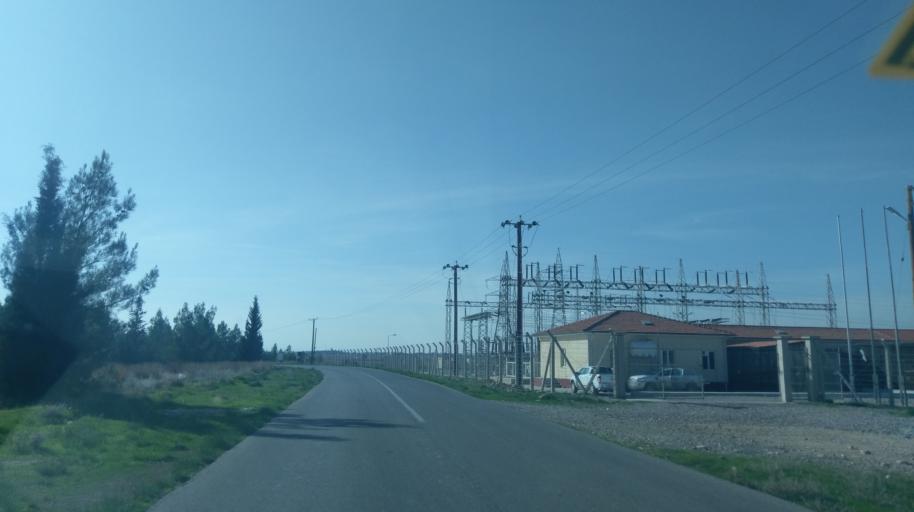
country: CY
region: Larnaka
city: Athienou
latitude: 35.1649
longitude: 33.5266
